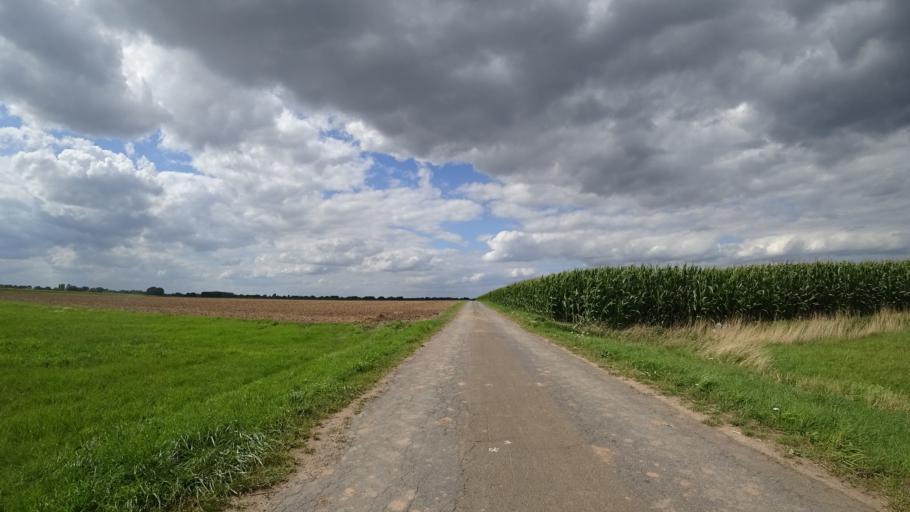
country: DE
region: Lower Saxony
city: Raddestorf
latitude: 52.4329
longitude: 9.0265
